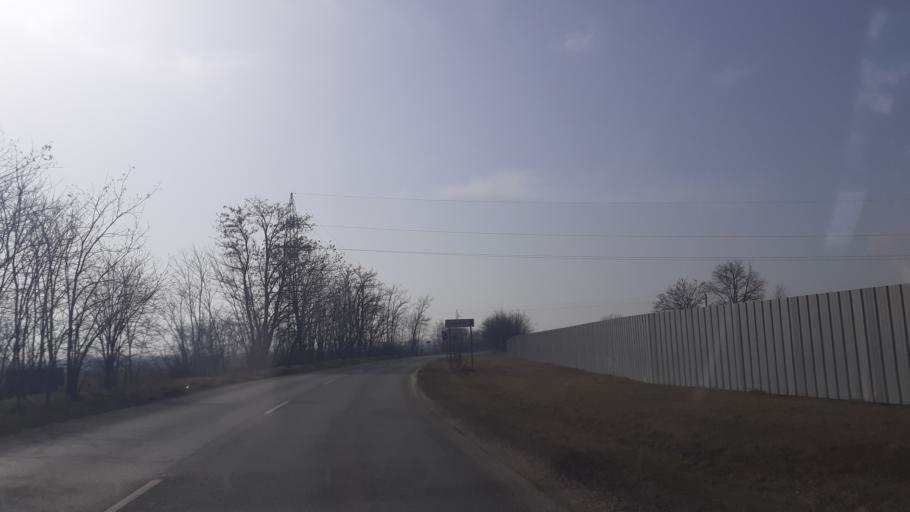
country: HU
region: Pest
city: Orkeny
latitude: 47.1448
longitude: 19.4599
